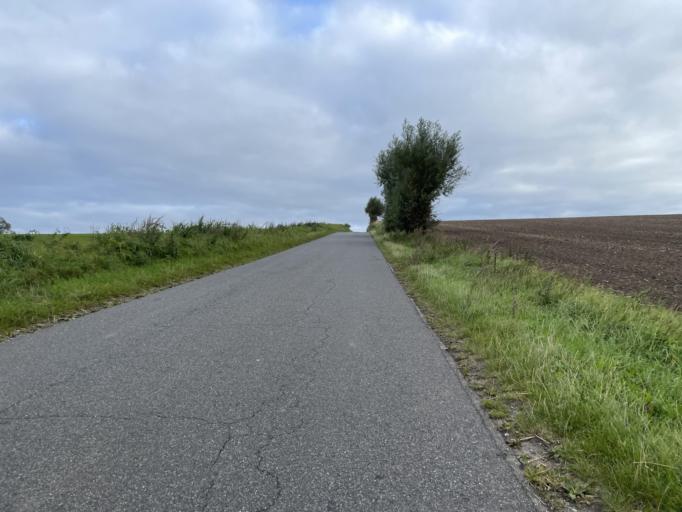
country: DK
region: South Denmark
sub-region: Kerteminde Kommune
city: Kerteminde
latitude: 55.4596
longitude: 10.6218
